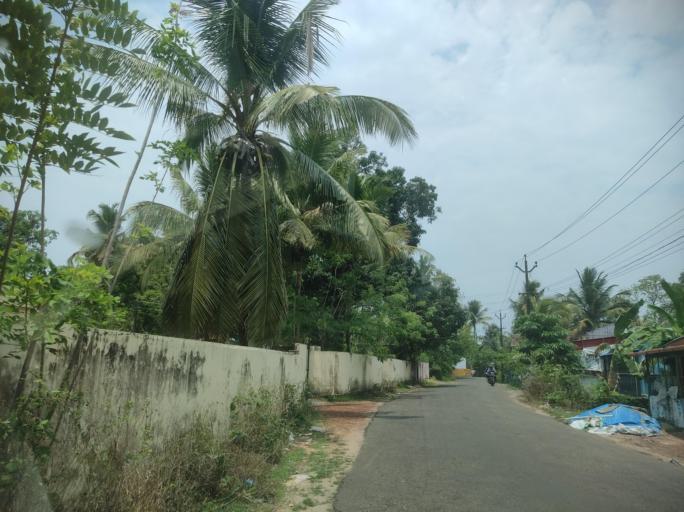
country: IN
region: Kerala
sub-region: Alappuzha
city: Kutiatodu
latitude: 9.7505
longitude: 76.3253
